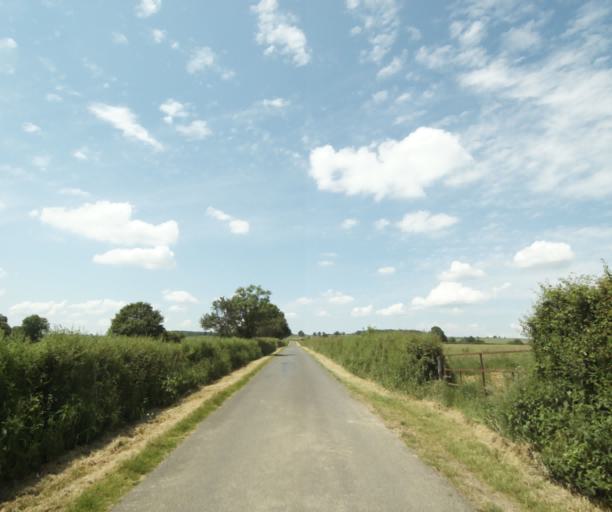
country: FR
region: Bourgogne
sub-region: Departement de Saone-et-Loire
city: Perrecy-les-Forges
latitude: 46.5805
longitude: 4.1495
